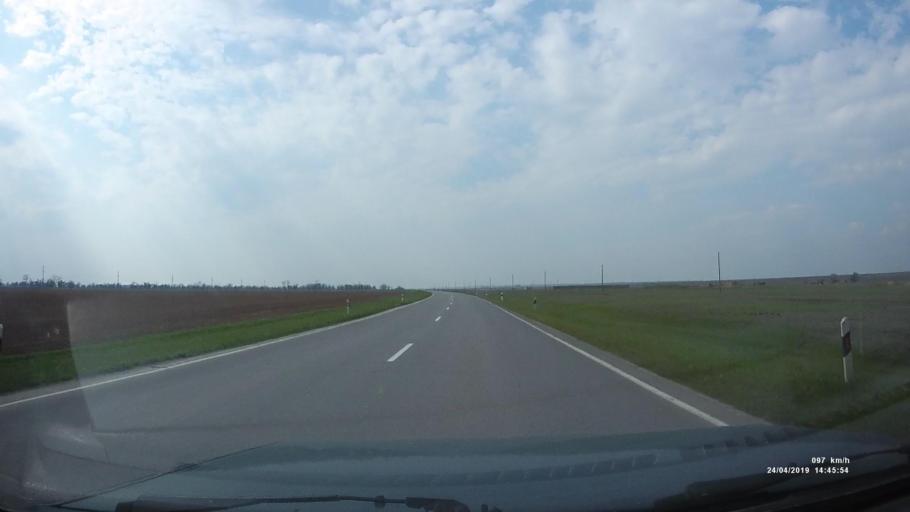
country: RU
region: Rostov
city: Remontnoye
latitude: 46.4769
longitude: 43.7991
